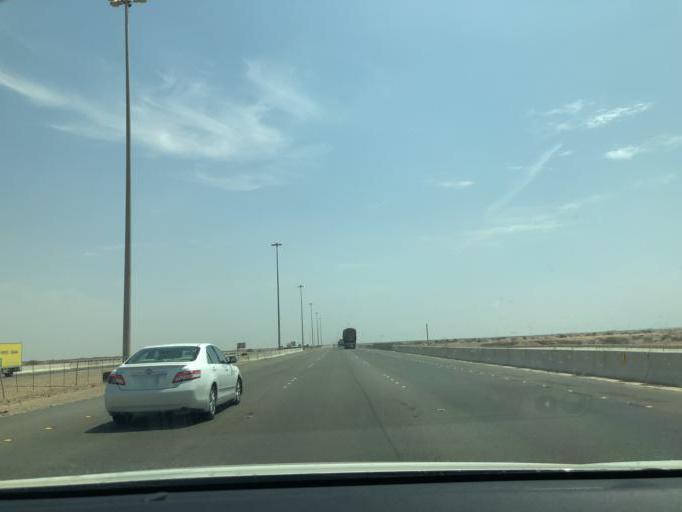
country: SA
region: Makkah
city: Rabigh
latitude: 22.2582
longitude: 39.1186
